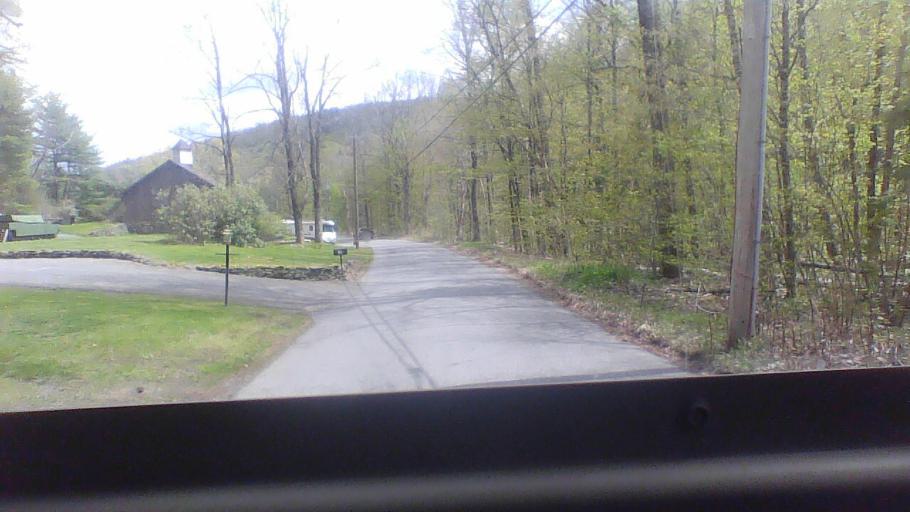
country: US
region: Massachusetts
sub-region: Franklin County
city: Buckland
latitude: 42.5831
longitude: -72.8298
